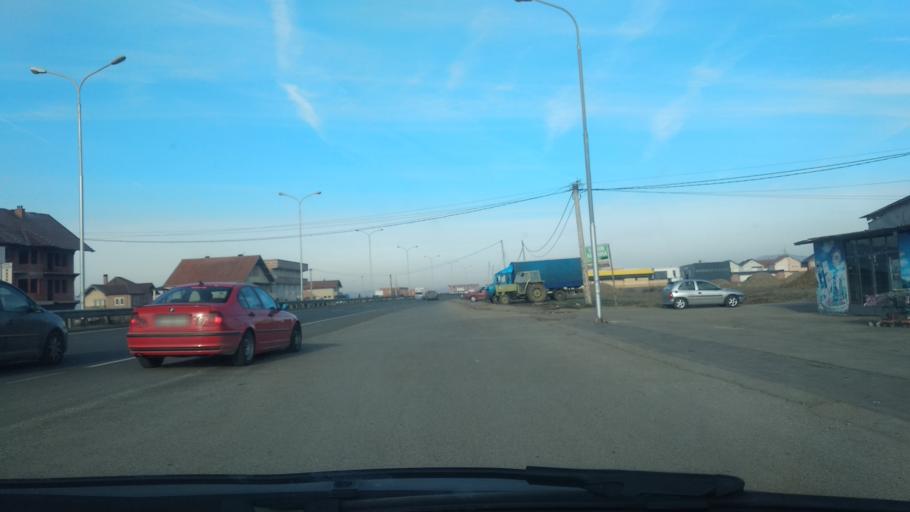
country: XK
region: Pristina
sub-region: Komuna e Obiliqit
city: Obiliq
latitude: 42.7409
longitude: 21.0518
